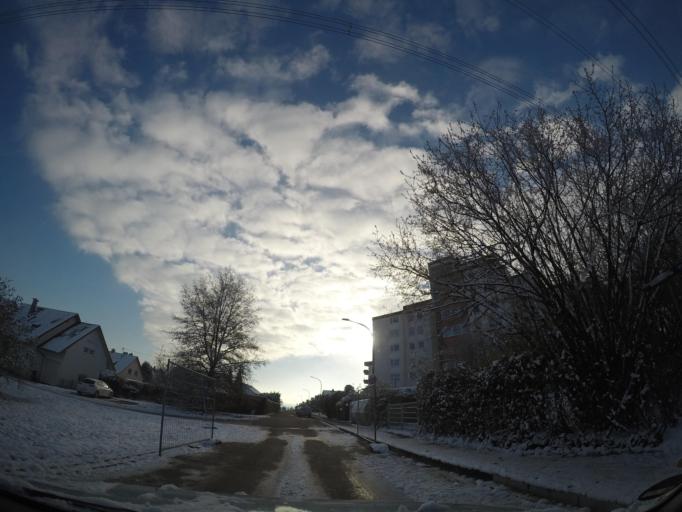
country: DE
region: Bavaria
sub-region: Swabia
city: Senden
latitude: 48.3178
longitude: 10.0620
